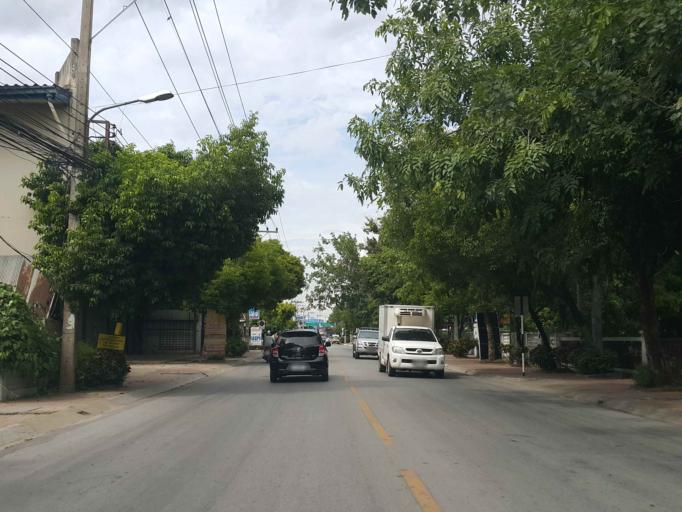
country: TH
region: Lamphun
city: Lamphun
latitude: 18.5843
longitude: 99.0094
